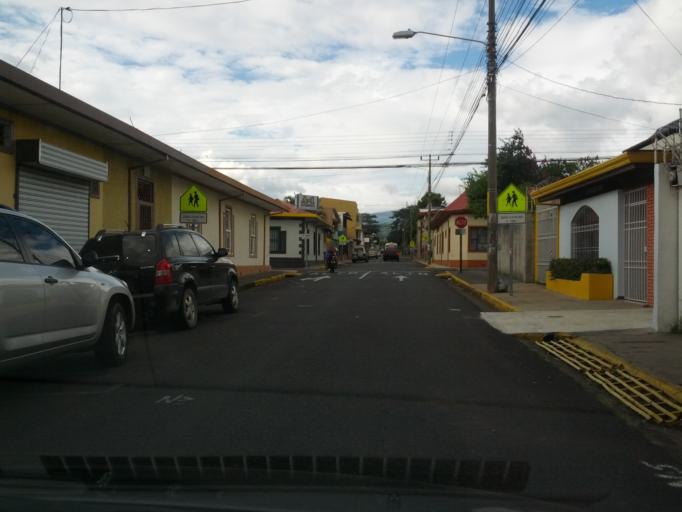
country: CR
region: Alajuela
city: Alajuela
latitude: 10.0182
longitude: -84.2112
